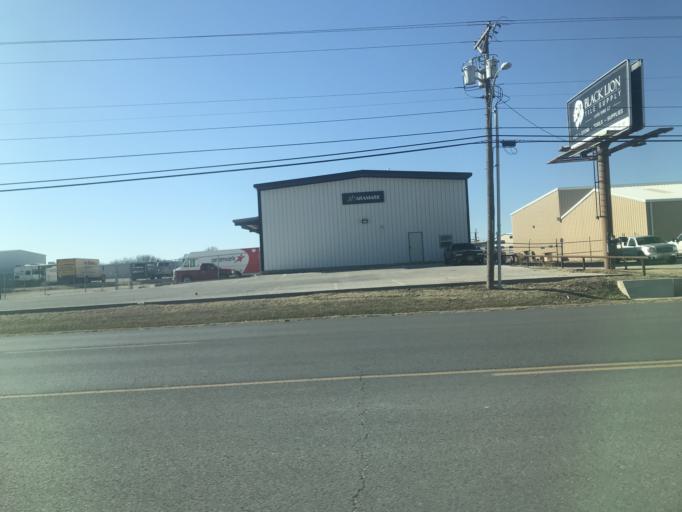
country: US
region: Texas
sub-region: Taylor County
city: Abilene
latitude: 32.4114
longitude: -99.7424
